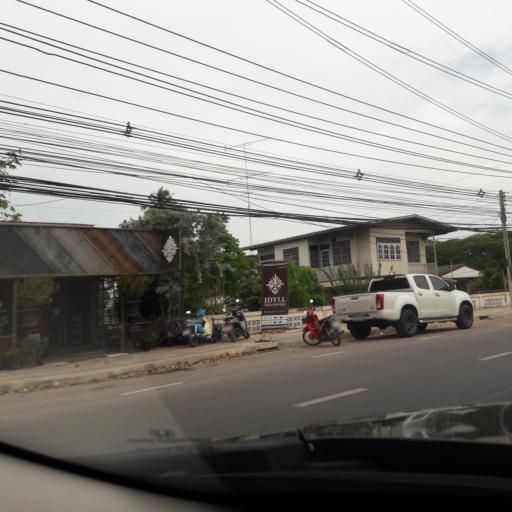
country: TH
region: Ratchaburi
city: Damnoen Saduak
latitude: 13.5410
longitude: 99.9643
